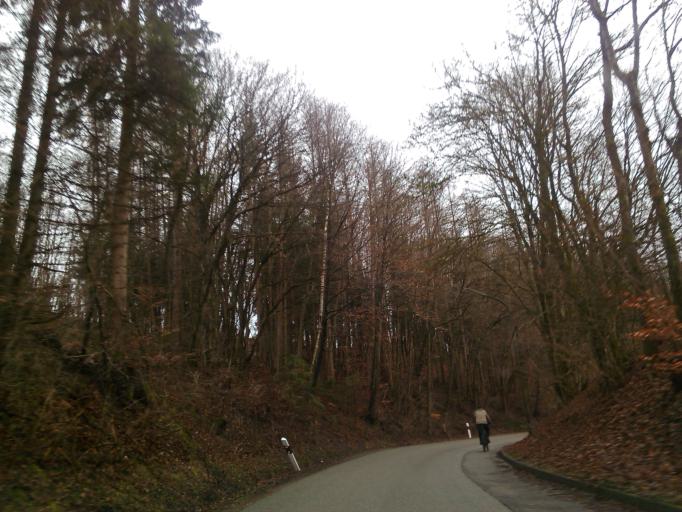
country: DE
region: Bavaria
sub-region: Upper Bavaria
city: Starnberg
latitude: 48.0311
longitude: 11.3563
